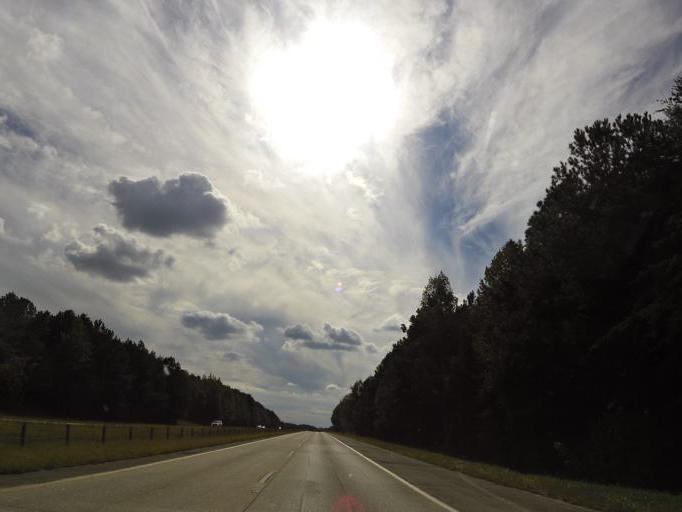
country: US
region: Georgia
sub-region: Cherokee County
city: Ball Ground
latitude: 34.3090
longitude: -84.4142
